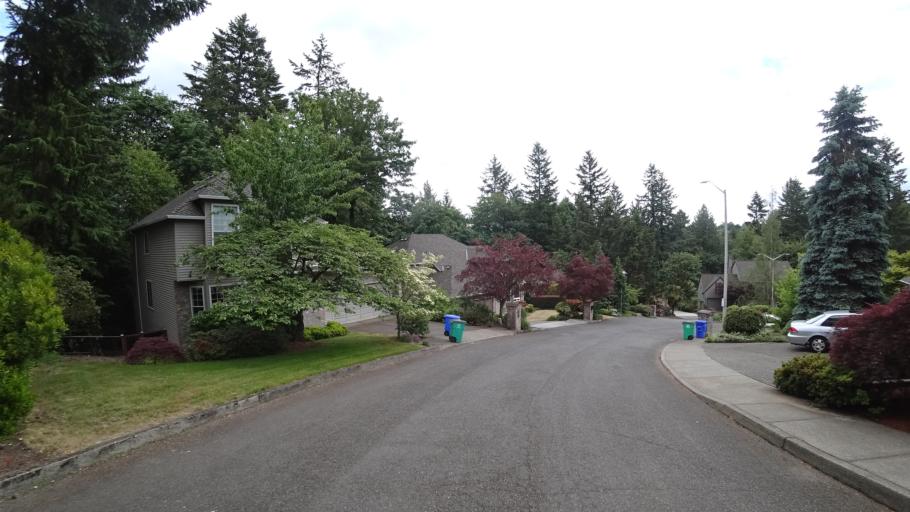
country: US
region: Oregon
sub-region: Clackamas County
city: Lake Oswego
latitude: 45.4482
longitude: -122.7020
